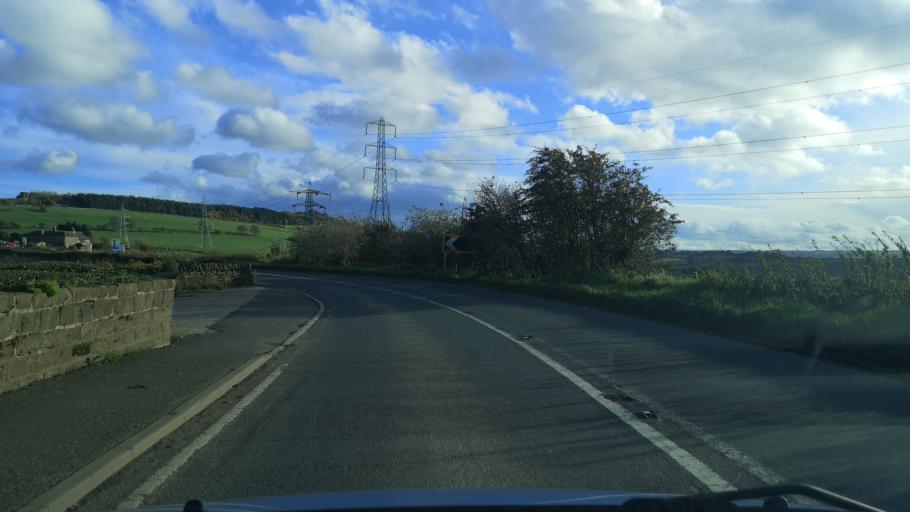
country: GB
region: England
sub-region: Kirklees
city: Mirfield
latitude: 53.6538
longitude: -1.6963
